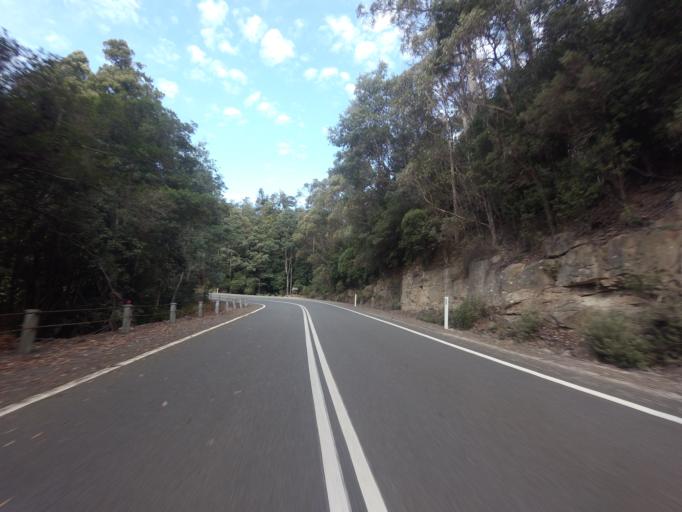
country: AU
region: Tasmania
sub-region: Meander Valley
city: Deloraine
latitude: -41.6536
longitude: 146.7199
